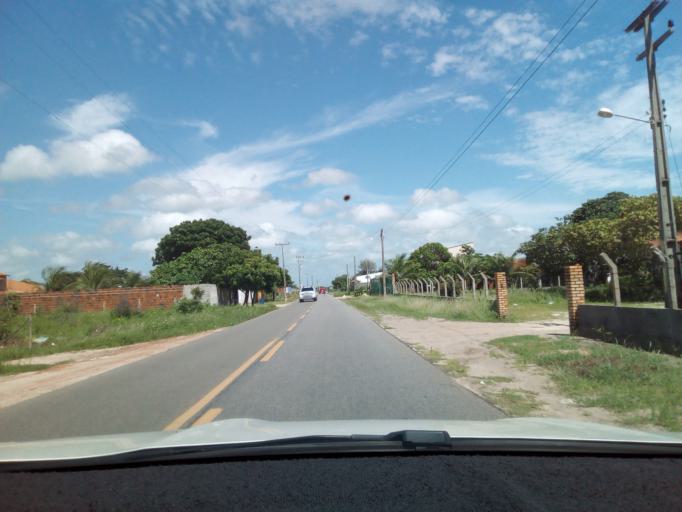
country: BR
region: Ceara
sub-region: Beberibe
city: Beberibe
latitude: -4.1851
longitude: -38.1035
